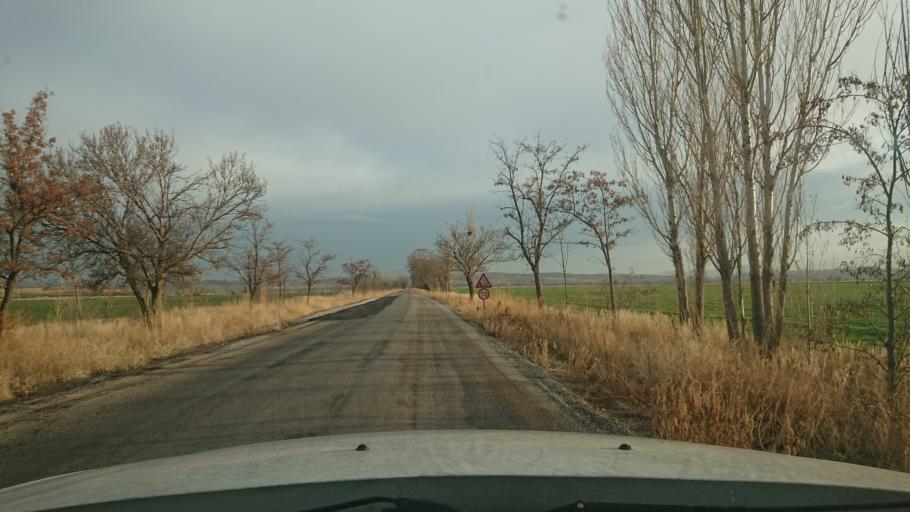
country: TR
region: Aksaray
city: Yesilova
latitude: 38.4624
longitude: 33.8418
